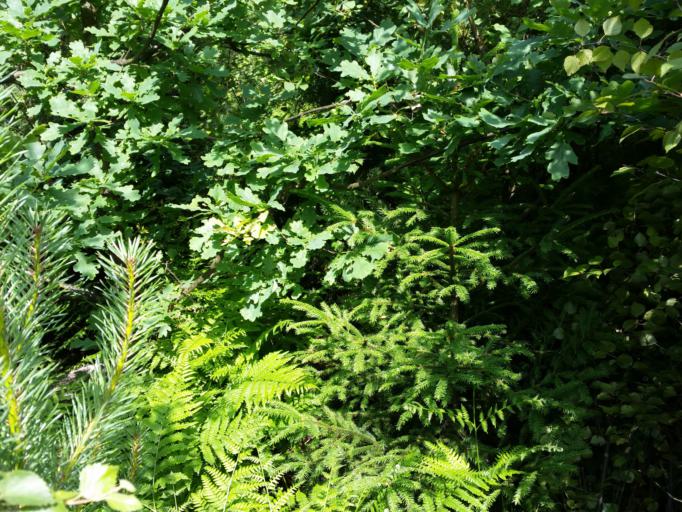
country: SE
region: Kronoberg
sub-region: Alvesta Kommun
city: Vislanda
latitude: 56.7239
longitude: 14.3629
